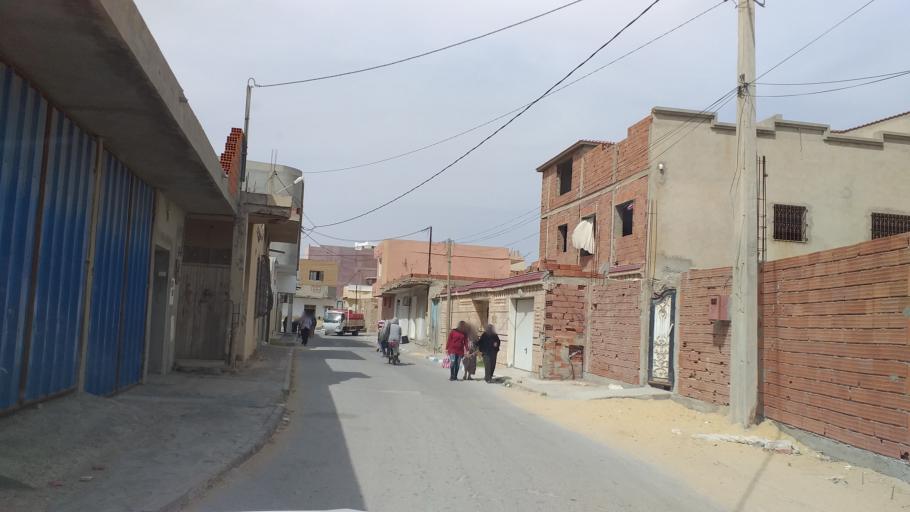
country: TN
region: Qabis
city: Gabes
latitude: 33.9386
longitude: 10.0633
